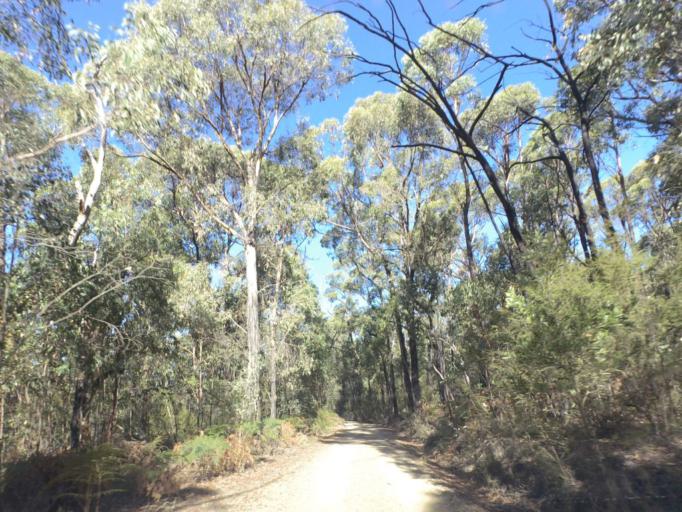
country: AU
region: Victoria
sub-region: Murrindindi
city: Kinglake West
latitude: -37.4628
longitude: 145.3806
